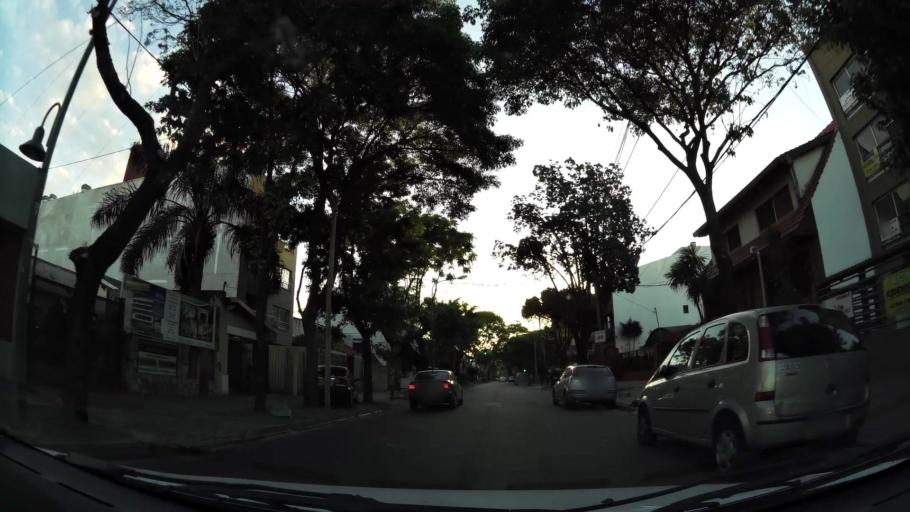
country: AR
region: Buenos Aires
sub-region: Partido de Vicente Lopez
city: Olivos
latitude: -34.5314
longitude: -58.5067
